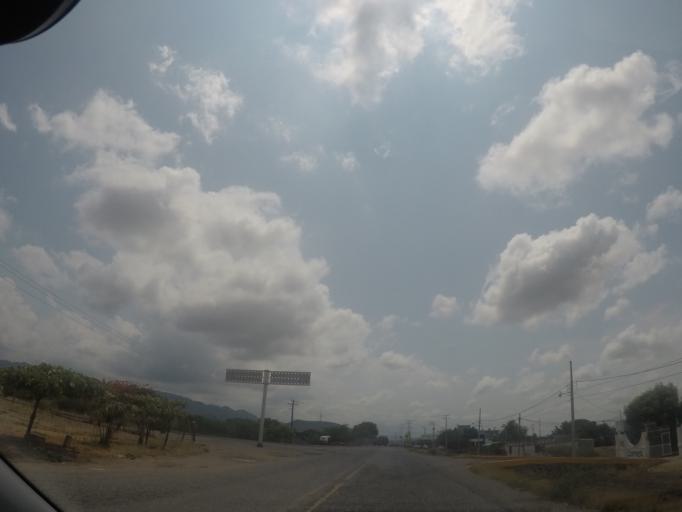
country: MX
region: Oaxaca
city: El Espinal
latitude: 16.5490
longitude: -94.9475
